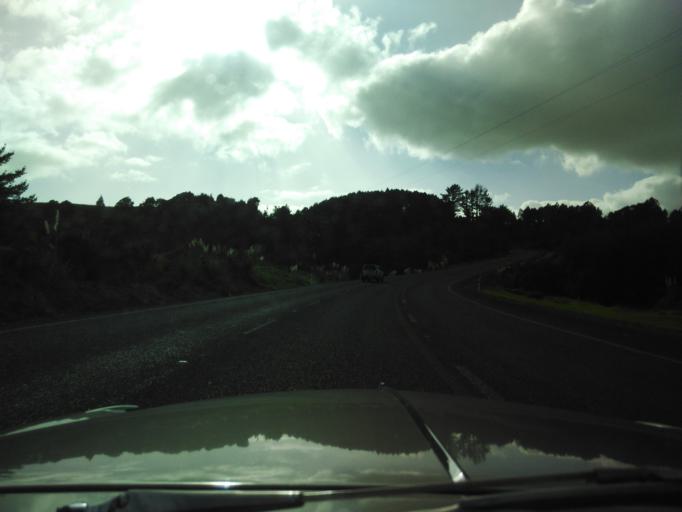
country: NZ
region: Auckland
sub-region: Auckland
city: Wellsford
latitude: -36.1900
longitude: 174.4507
